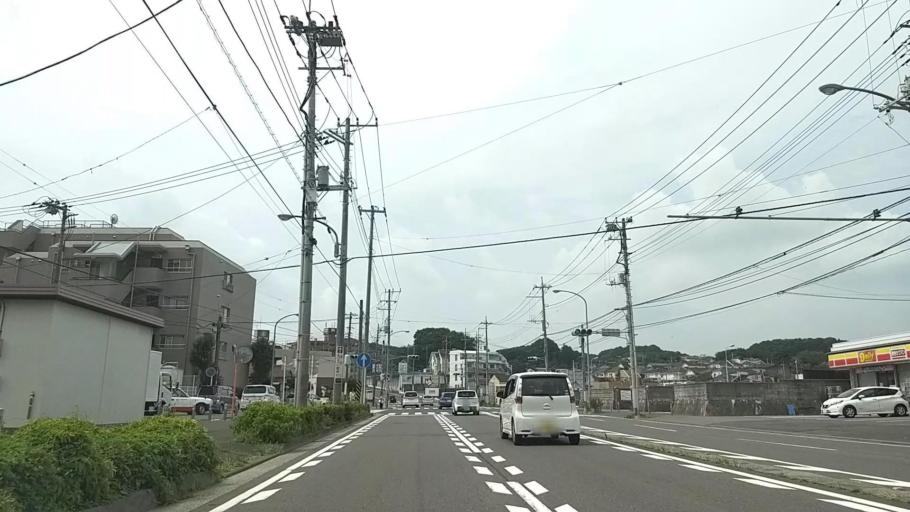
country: JP
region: Kanagawa
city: Minami-rinkan
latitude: 35.5085
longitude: 139.5441
